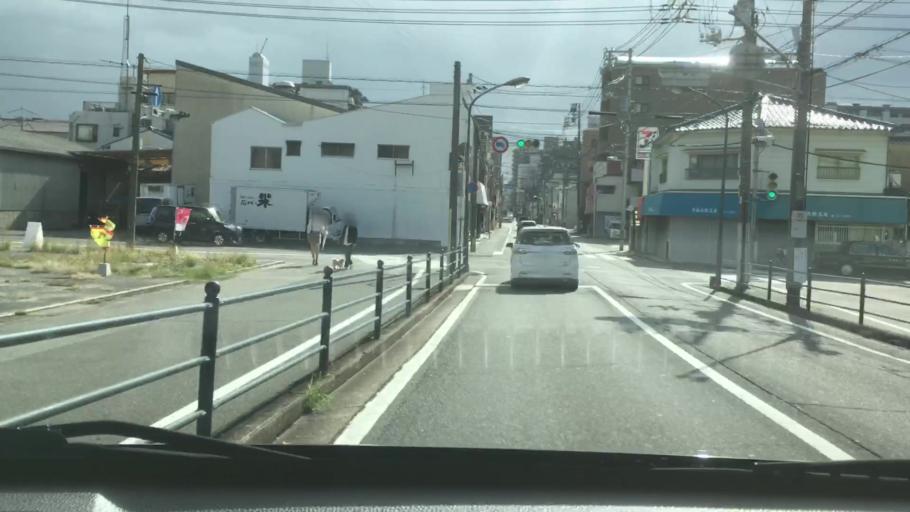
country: JP
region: Hiroshima
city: Hiroshima-shi
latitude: 34.3980
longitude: 132.4351
